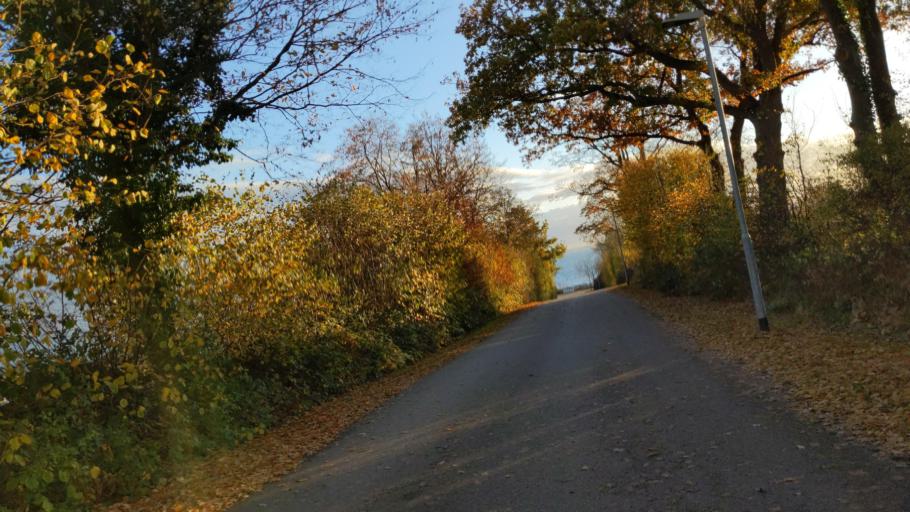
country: DE
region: Schleswig-Holstein
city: Neustadt in Holstein
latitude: 54.0900
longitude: 10.8312
